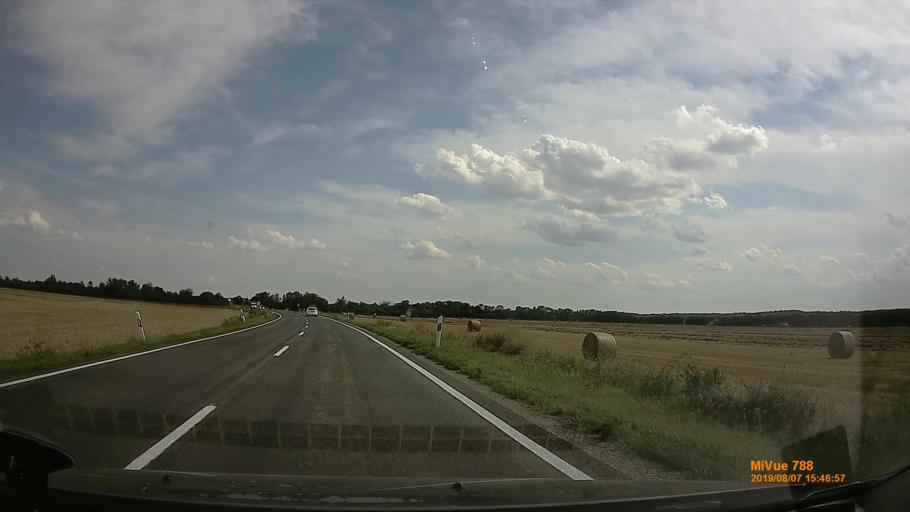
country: HU
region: Vas
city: Szombathely
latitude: 47.1781
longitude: 16.6229
